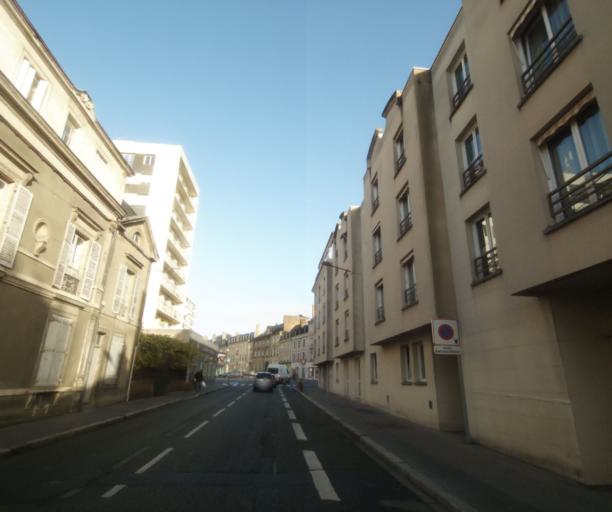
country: FR
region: Pays de la Loire
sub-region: Departement de la Sarthe
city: Le Mans
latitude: 48.0034
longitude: 0.2026
